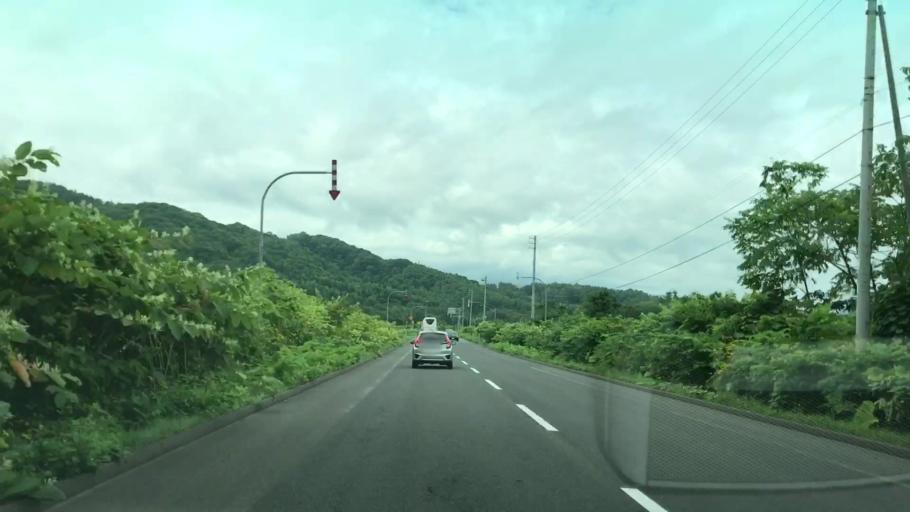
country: JP
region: Hokkaido
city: Niseko Town
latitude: 42.9468
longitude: 140.8453
